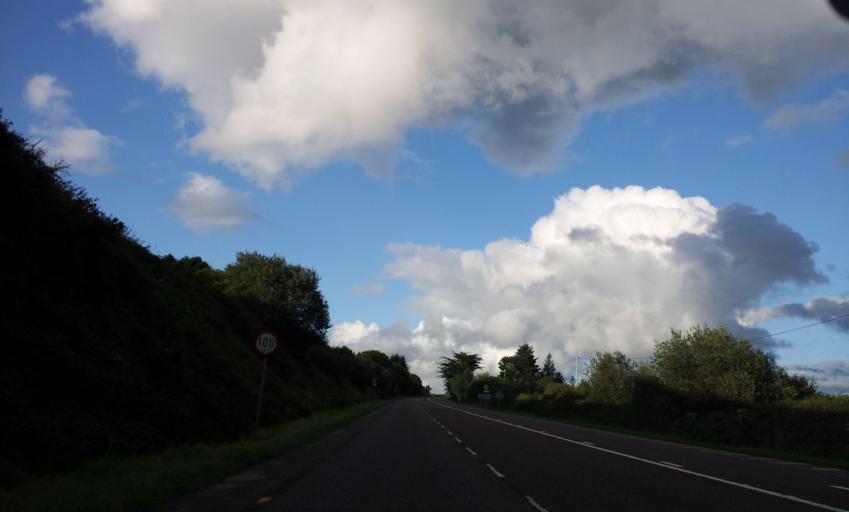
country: IE
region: Munster
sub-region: Ciarrai
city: Castleisland
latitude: 52.2666
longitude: -9.4248
